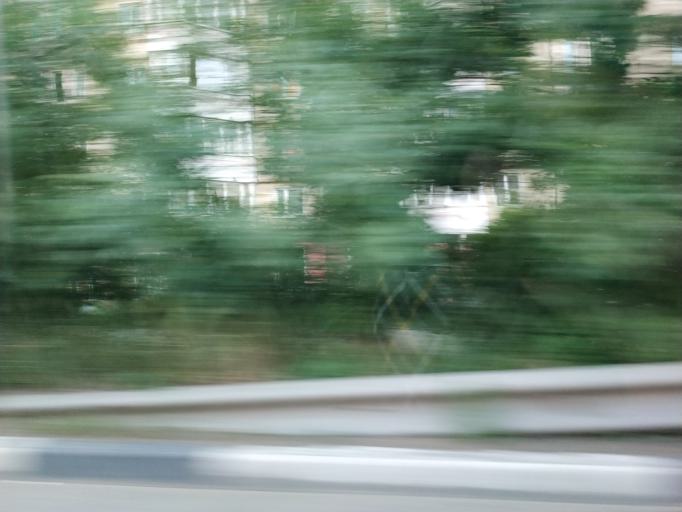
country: RU
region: Moskovskaya
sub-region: Shchelkovskiy Rayon
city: Grebnevo
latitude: 55.9565
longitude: 38.0637
